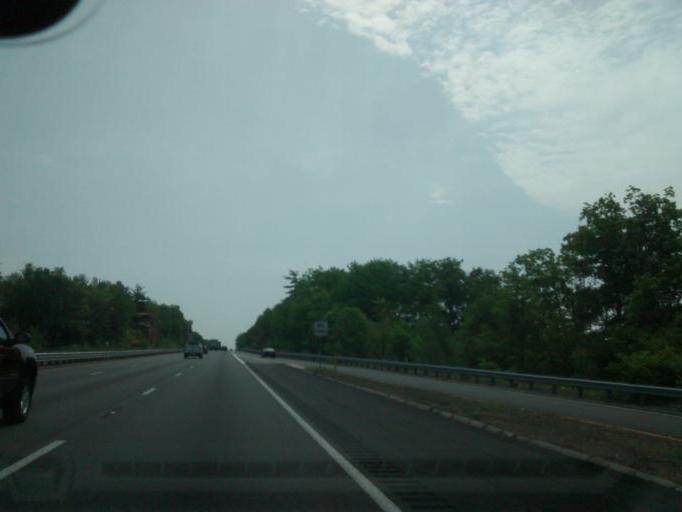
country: US
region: Massachusetts
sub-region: Worcester County
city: Milford
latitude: 42.1644
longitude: -71.5043
